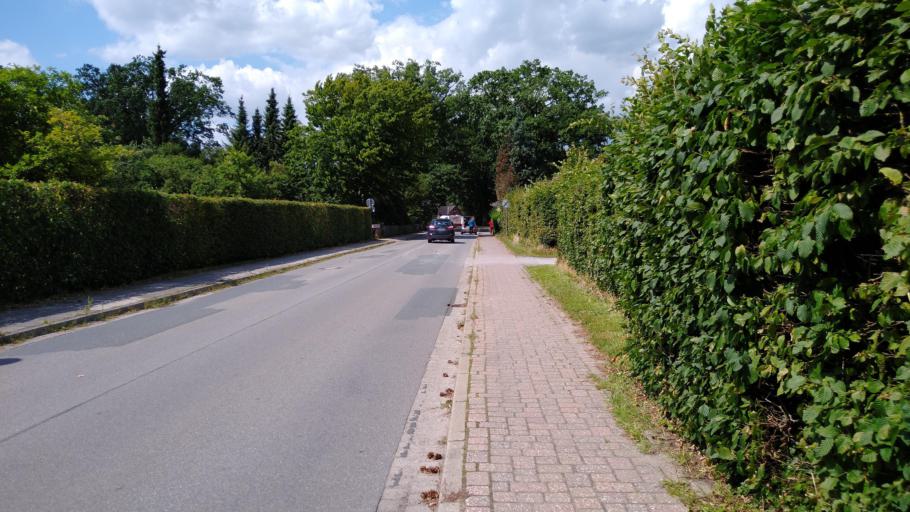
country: DE
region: Lower Saxony
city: Wienhausen
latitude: 52.5788
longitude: 10.1931
